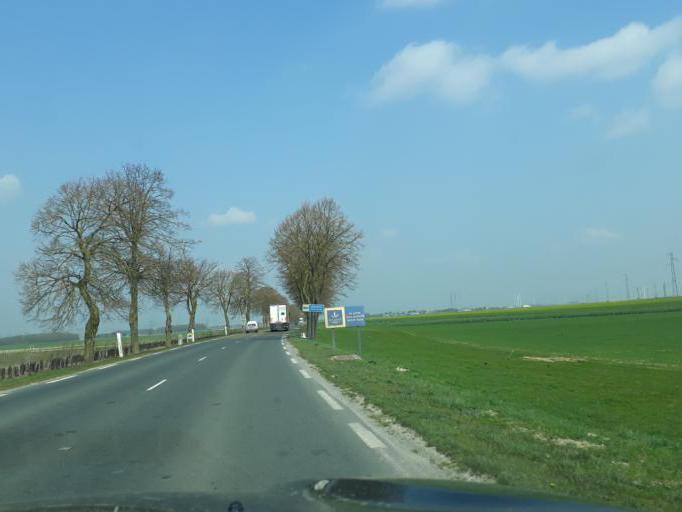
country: FR
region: Centre
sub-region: Departement du Loiret
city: Artenay
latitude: 48.0889
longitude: 1.8656
